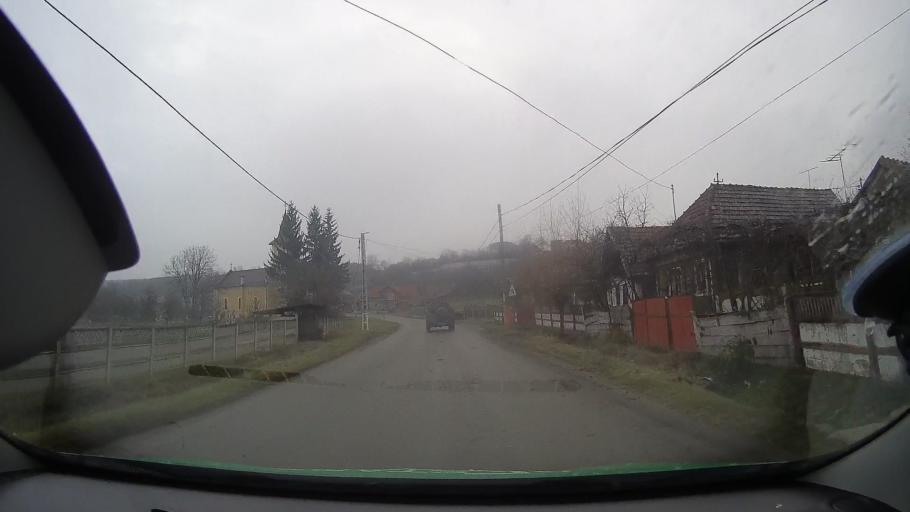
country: RO
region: Alba
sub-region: Comuna Noslac
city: Noslac
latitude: 46.4104
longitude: 23.9413
